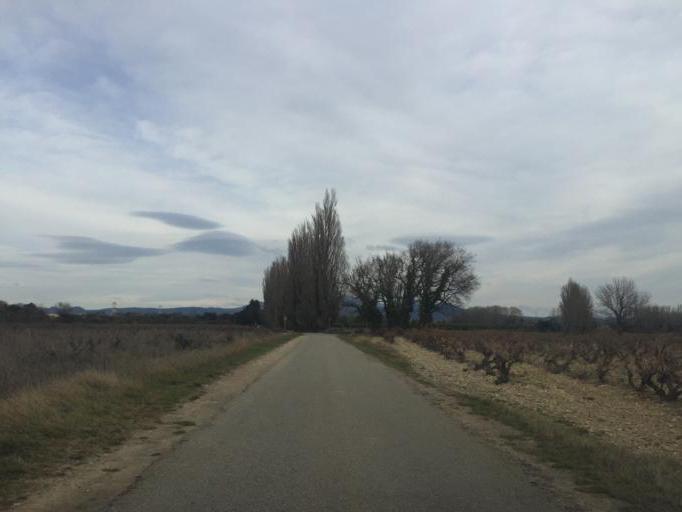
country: FR
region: Provence-Alpes-Cote d'Azur
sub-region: Departement du Vaucluse
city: Camaret-sur-Aigues
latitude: 44.1615
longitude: 4.8899
